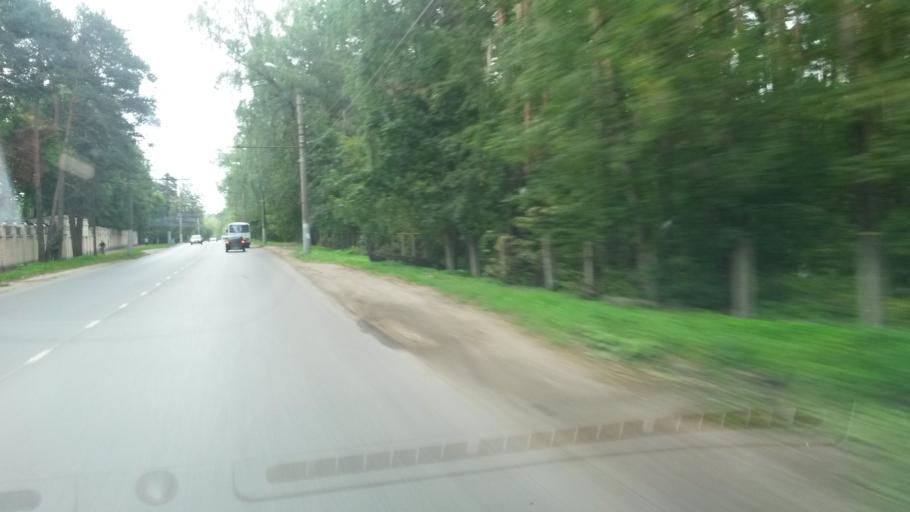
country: RU
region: Ivanovo
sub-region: Gorod Ivanovo
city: Ivanovo
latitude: 57.0254
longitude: 40.9401
